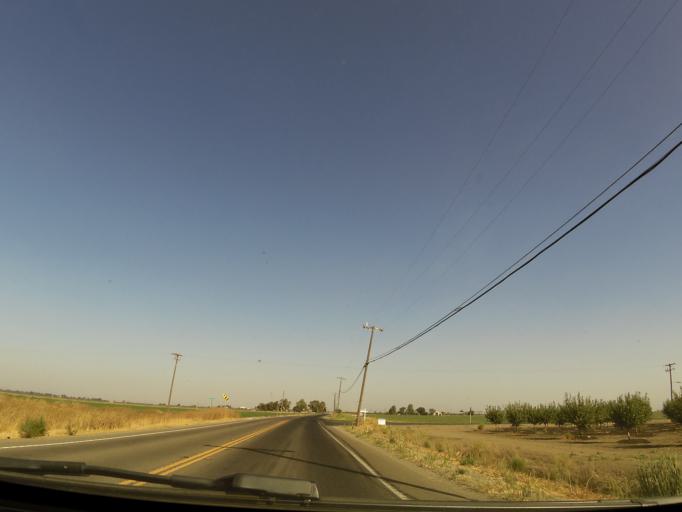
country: US
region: California
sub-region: San Joaquin County
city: Taft Mosswood
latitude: 37.8773
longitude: -121.3682
